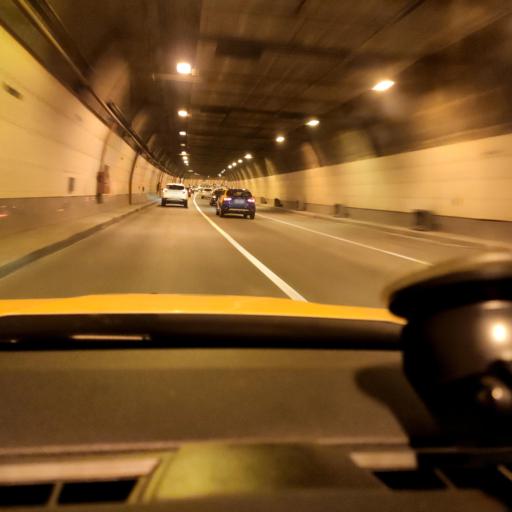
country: RU
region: Moscow
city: Strogino
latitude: 55.7742
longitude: 37.4038
